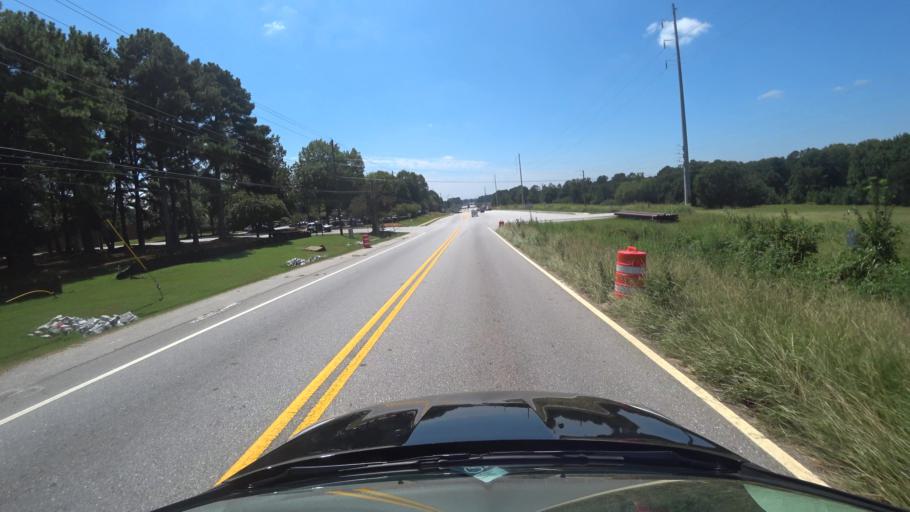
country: US
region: Georgia
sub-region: Newton County
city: Oxford
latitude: 33.6215
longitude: -83.8377
